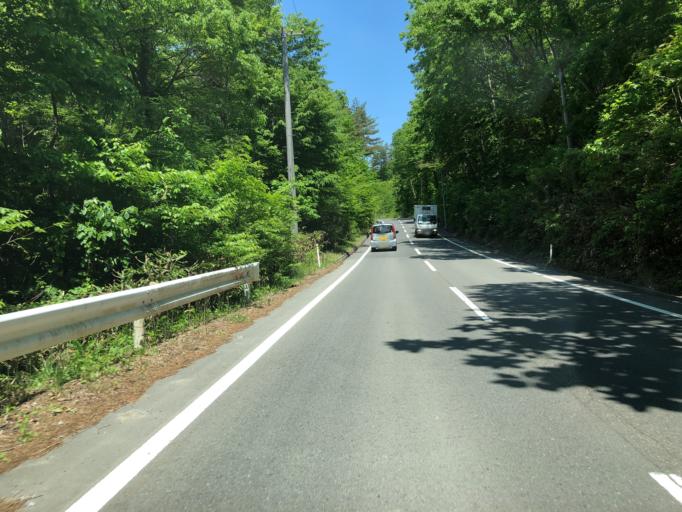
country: JP
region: Fukushima
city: Funehikimachi-funehiki
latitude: 37.5061
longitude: 140.7751
